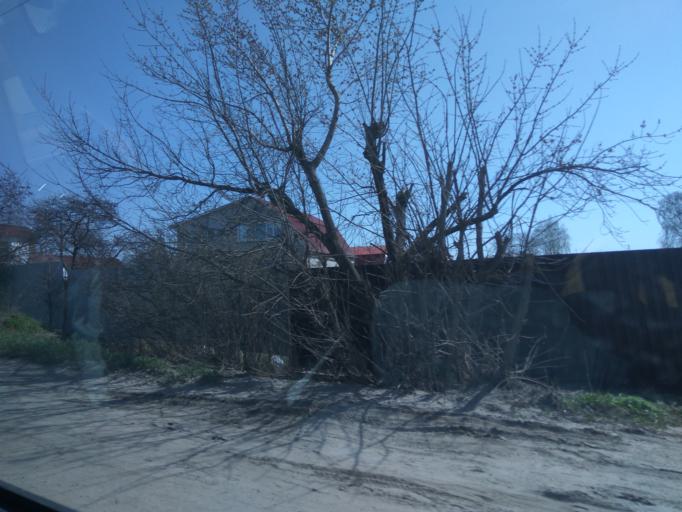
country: RU
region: Moskovskaya
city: Ramenskoye
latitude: 55.5490
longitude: 38.2344
